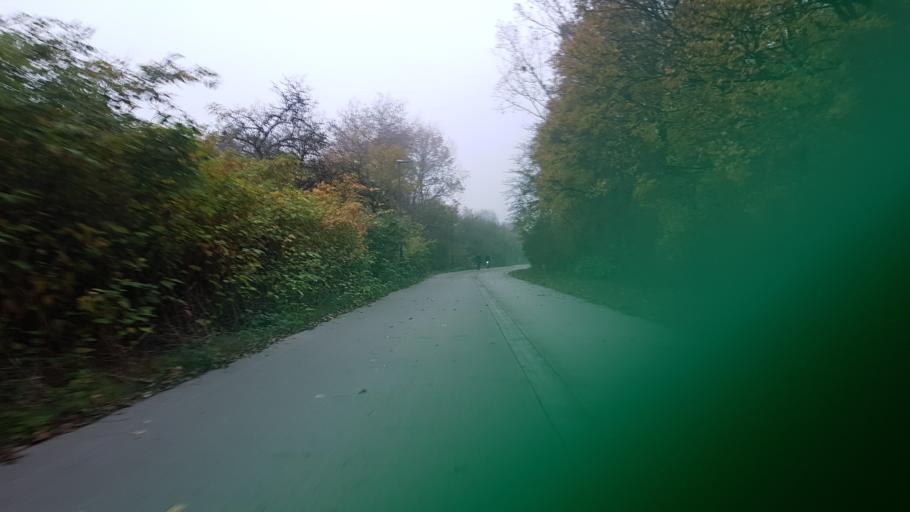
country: DE
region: Bavaria
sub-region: Upper Bavaria
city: Pasing
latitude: 48.1510
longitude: 11.4855
